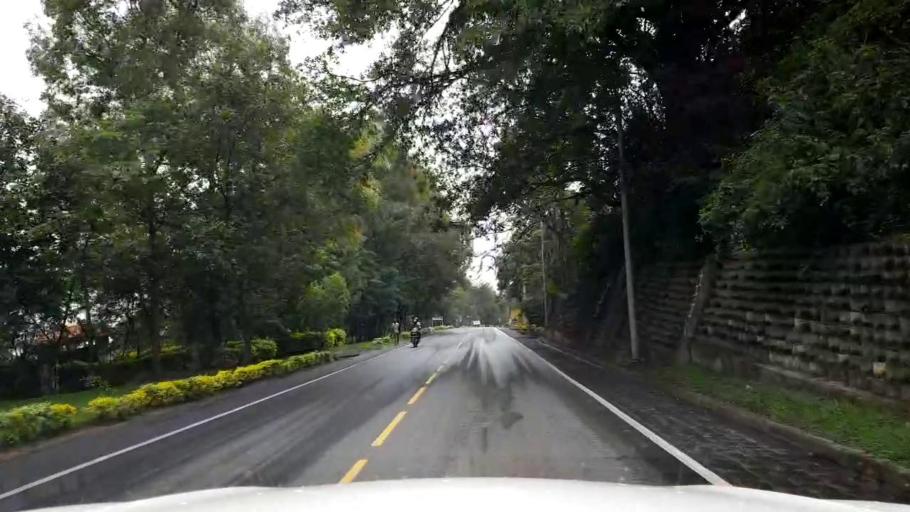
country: RW
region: Western Province
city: Gisenyi
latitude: -1.7043
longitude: 29.2682
